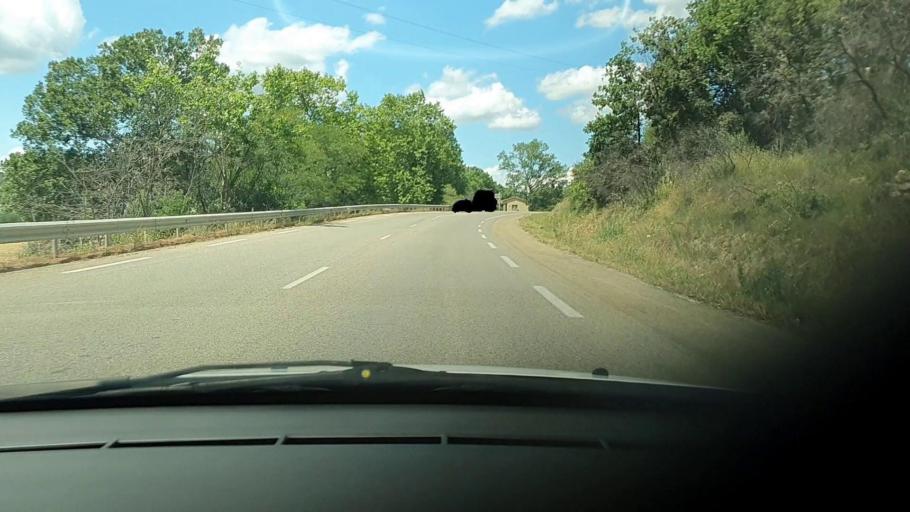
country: FR
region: Languedoc-Roussillon
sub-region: Departement du Gard
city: Montaren-et-Saint-Mediers
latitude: 44.0354
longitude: 4.3619
